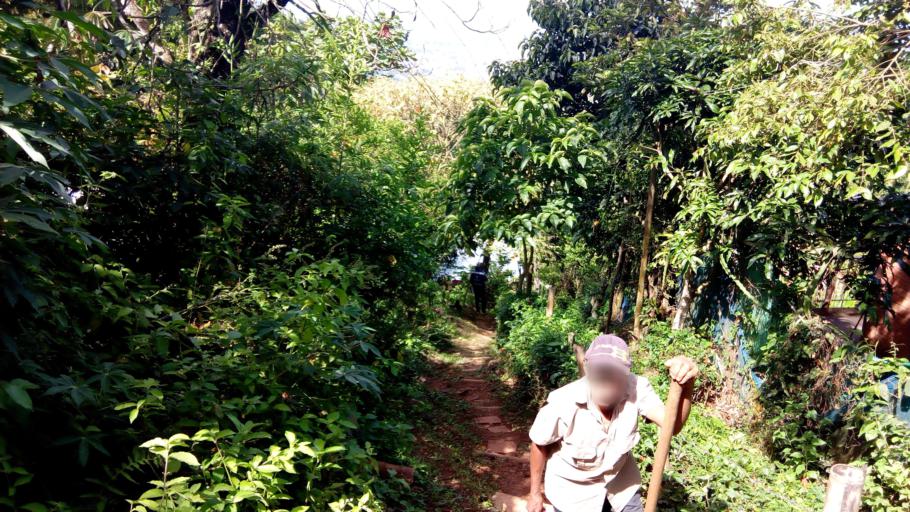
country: CO
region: Valle del Cauca
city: Cali
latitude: 3.4389
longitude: -76.5947
